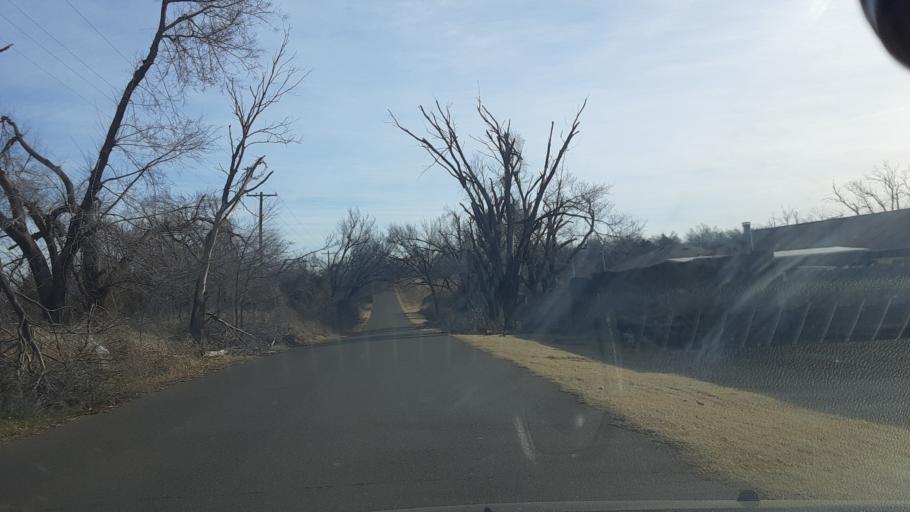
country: US
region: Oklahoma
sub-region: Logan County
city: Guthrie
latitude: 35.8924
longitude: -97.4151
